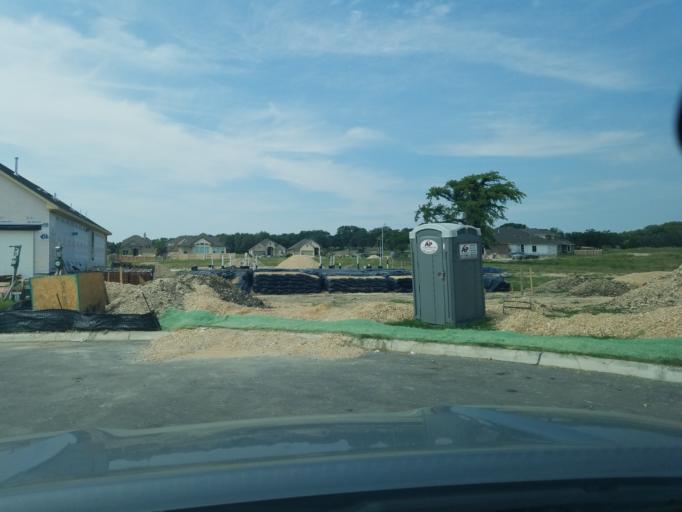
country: US
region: Texas
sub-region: Kendall County
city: Boerne
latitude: 29.7546
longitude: -98.7152
